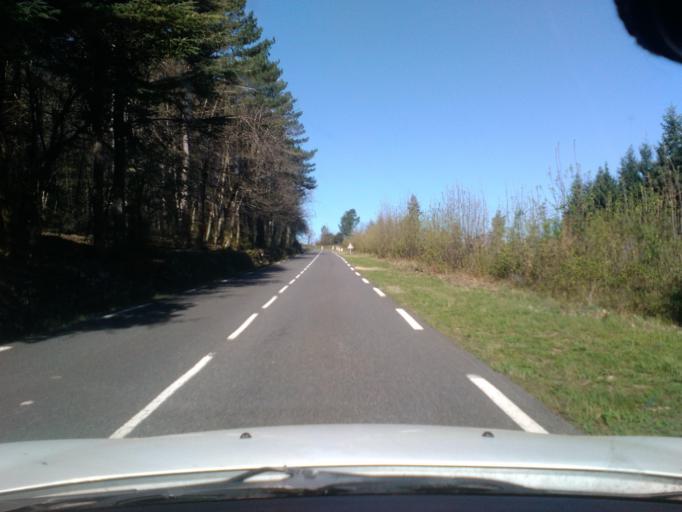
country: FR
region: Languedoc-Roussillon
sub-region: Departement du Gard
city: Saint-Jean-du-Gard
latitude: 44.1374
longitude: 3.8249
